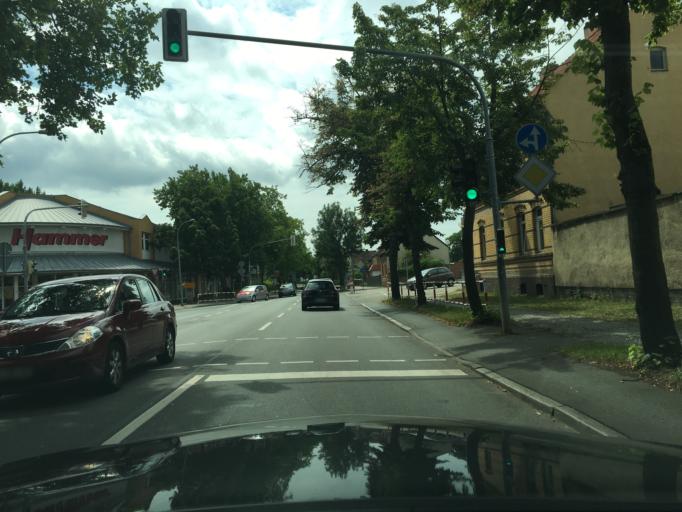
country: DE
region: Saxony-Anhalt
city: Wolfen
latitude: 51.6567
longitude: 12.2746
